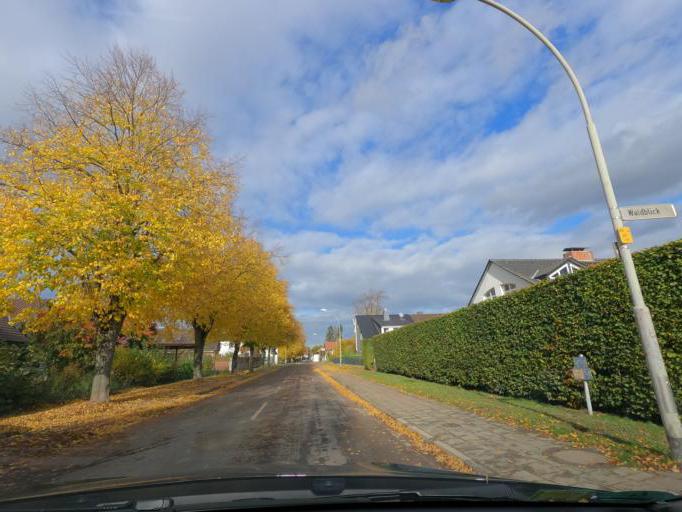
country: DE
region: Lower Saxony
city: Leiferde
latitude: 52.2060
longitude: 10.5227
